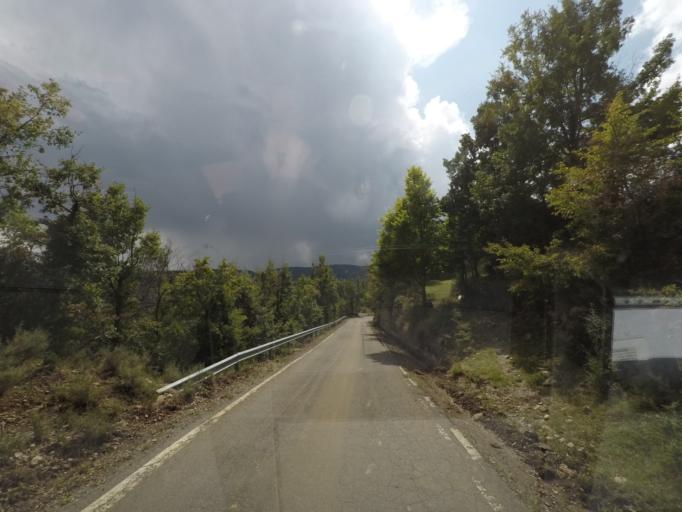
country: ES
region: Aragon
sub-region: Provincia de Huesca
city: Fiscal
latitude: 42.4136
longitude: -0.1212
